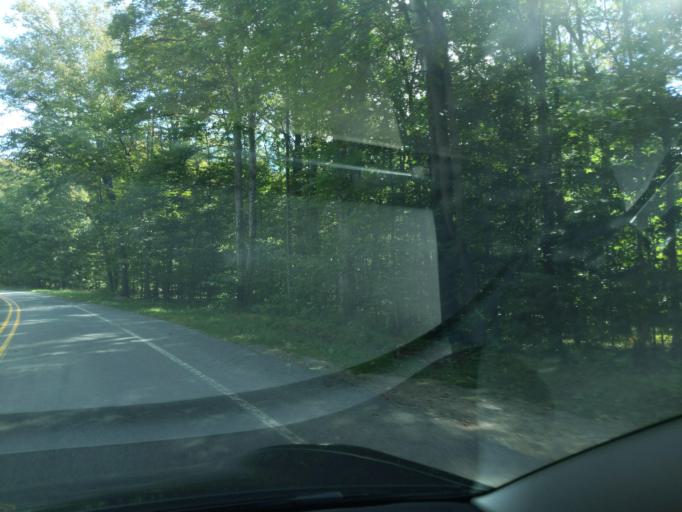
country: US
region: Michigan
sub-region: Antrim County
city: Bellaire
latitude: 45.0256
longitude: -85.2954
